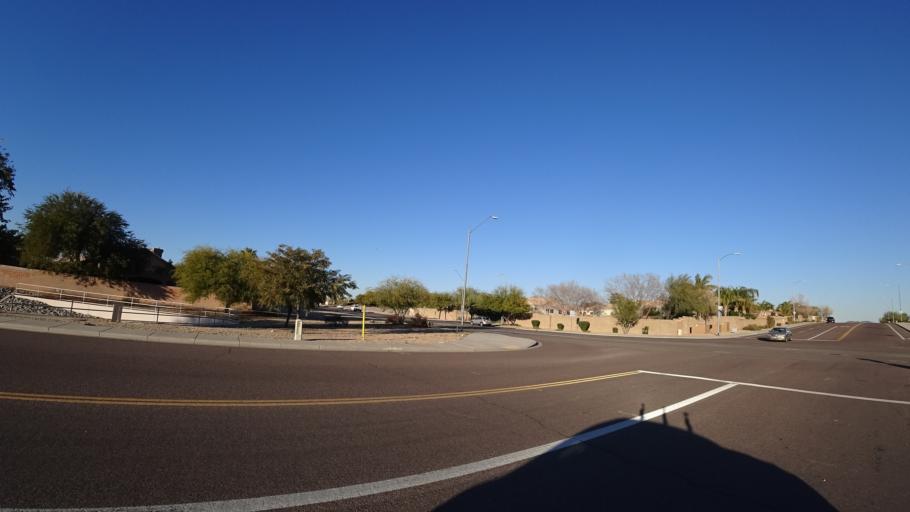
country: US
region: Arizona
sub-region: Maricopa County
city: Sun City West
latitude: 33.6744
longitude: -112.2904
